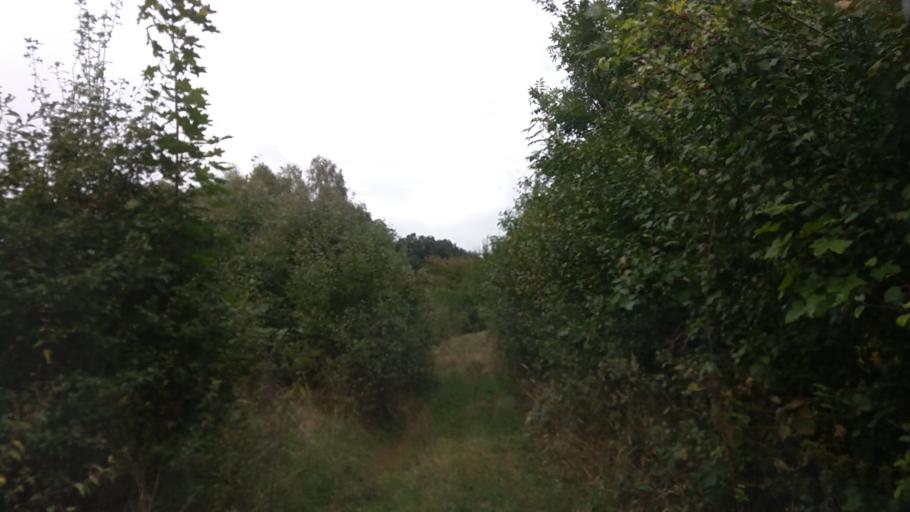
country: PL
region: West Pomeranian Voivodeship
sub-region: Powiat choszczenski
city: Bierzwnik
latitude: 52.9930
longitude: 15.6029
